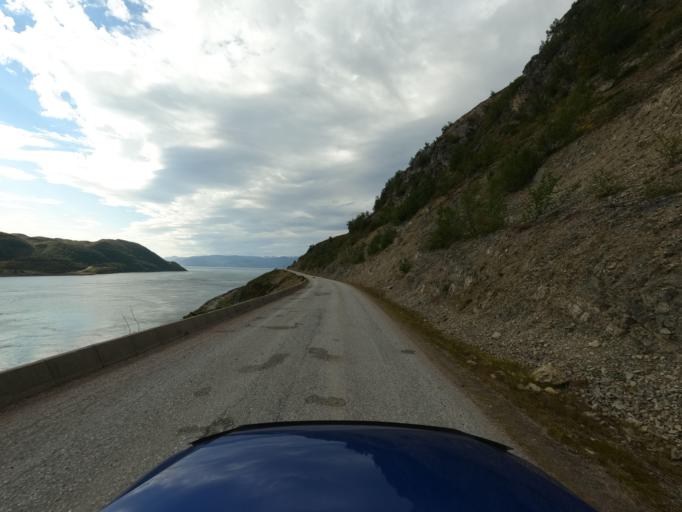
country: NO
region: Finnmark Fylke
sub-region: Kvalsund
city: Kvalsund
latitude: 70.5085
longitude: 23.9083
